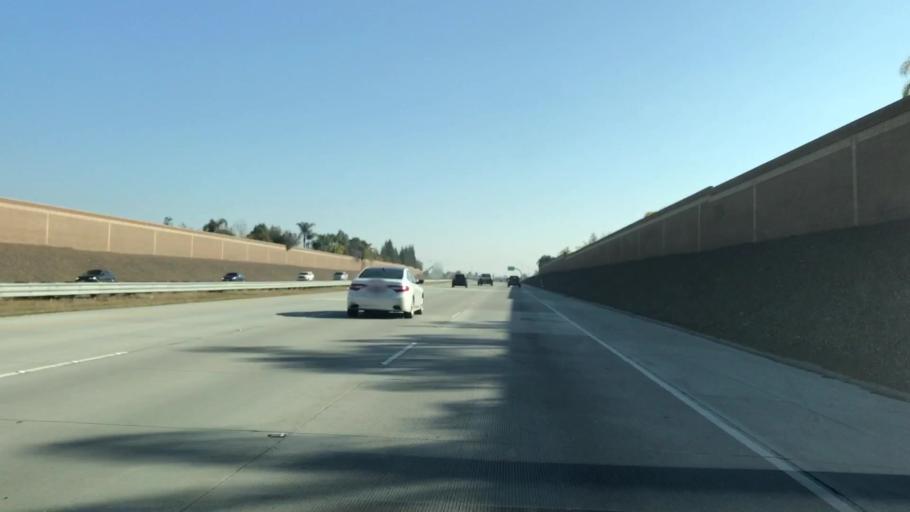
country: US
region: California
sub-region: Kern County
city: Greenacres
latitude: 35.3617
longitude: -119.1273
